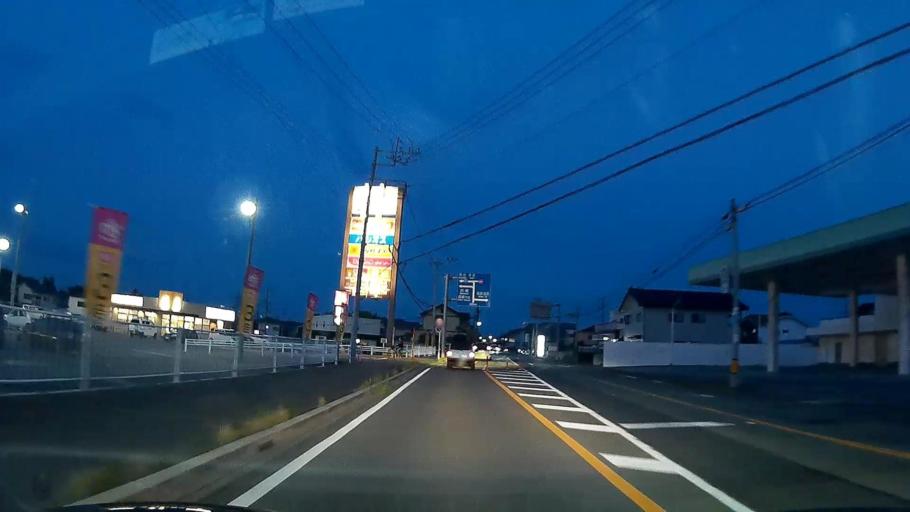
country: JP
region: Gunma
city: Takasaki
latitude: 36.3338
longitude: 138.9843
